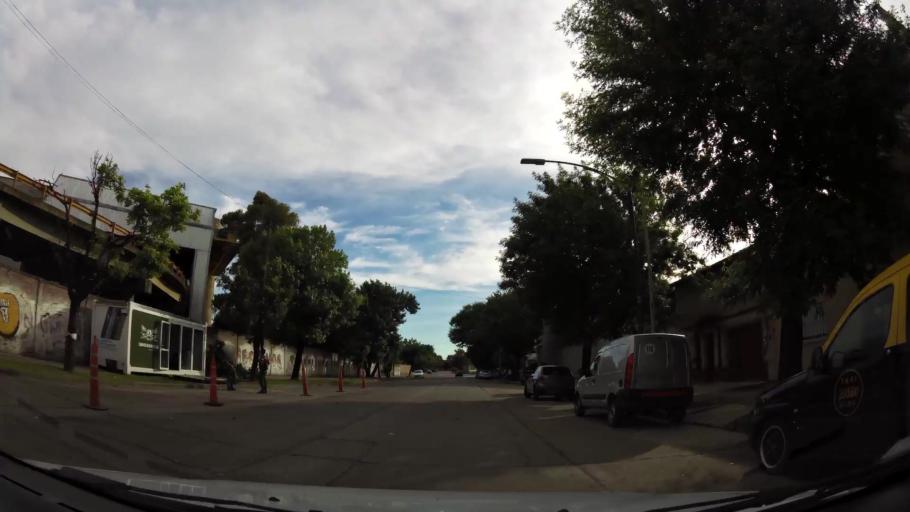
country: AR
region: Buenos Aires F.D.
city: Villa Lugano
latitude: -34.6496
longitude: -58.4564
